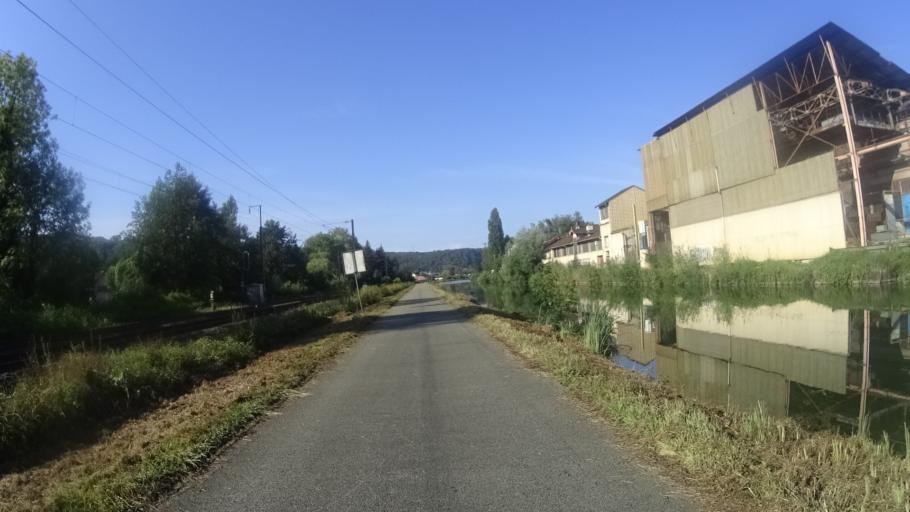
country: FR
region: Franche-Comte
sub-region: Departement du Doubs
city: Colombier-Fontaine
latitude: 47.4547
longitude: 6.6880
